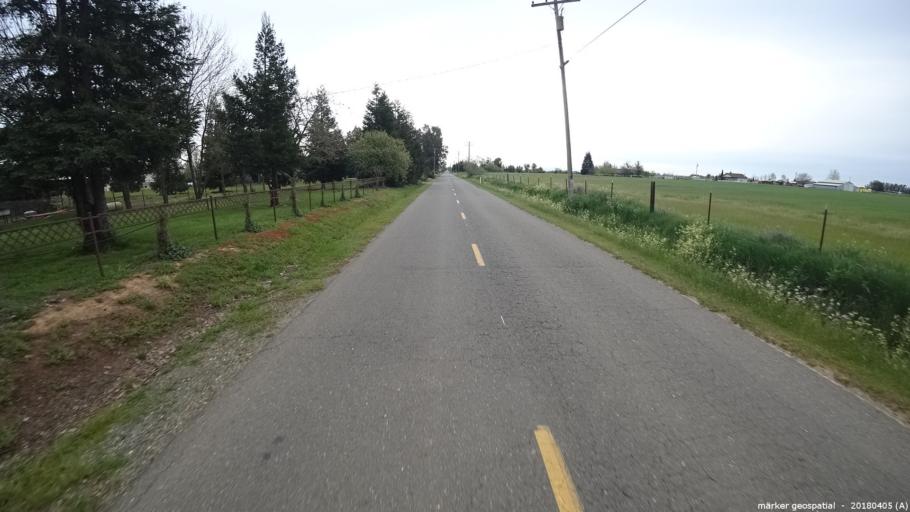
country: US
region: California
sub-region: Sacramento County
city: Herald
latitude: 38.2773
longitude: -121.2387
